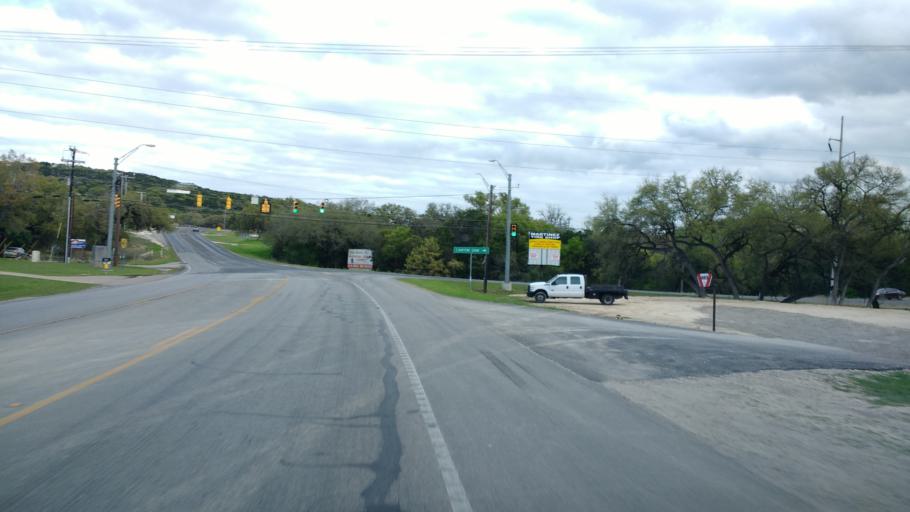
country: US
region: Texas
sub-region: Comal County
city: Canyon Lake
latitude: 29.8765
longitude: -98.1952
